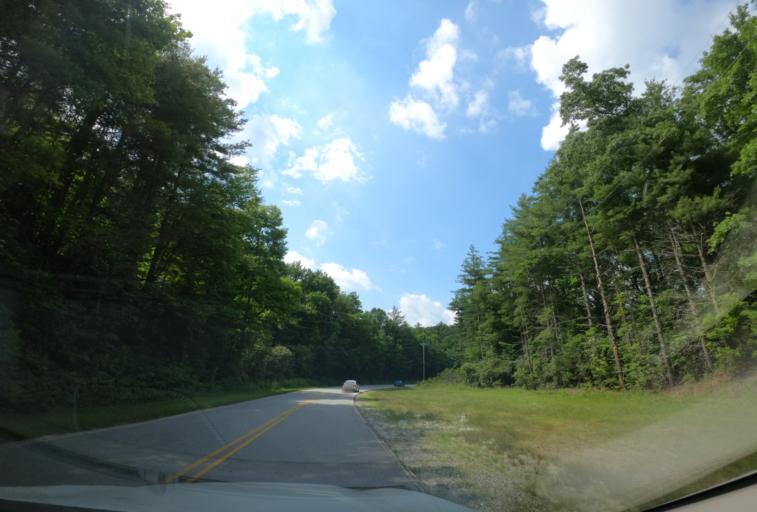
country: US
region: North Carolina
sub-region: Jackson County
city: Cullowhee
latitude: 35.0667
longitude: -83.0074
